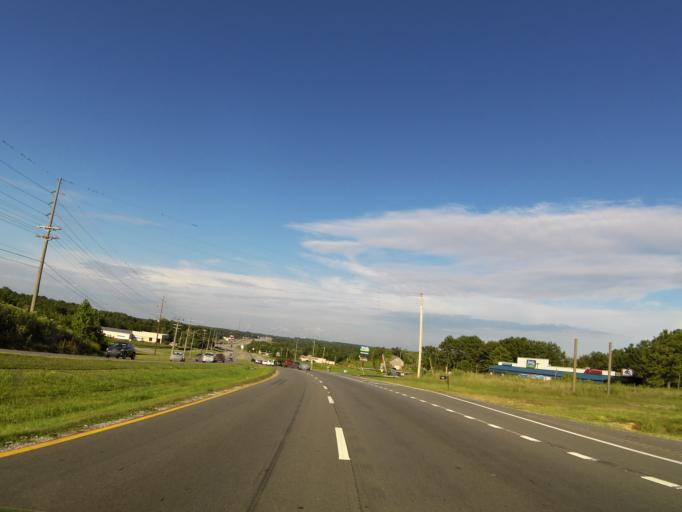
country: US
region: Alabama
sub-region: Lauderdale County
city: Killen
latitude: 34.8449
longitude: -87.5821
